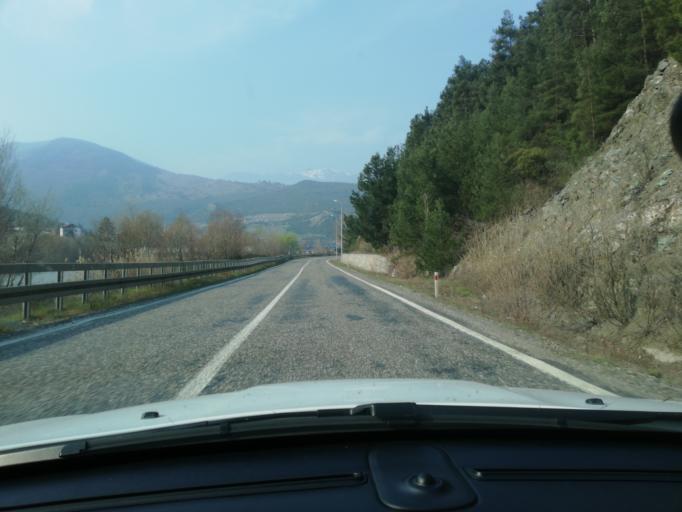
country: TR
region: Karabuk
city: Karabuk
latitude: 41.1574
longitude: 32.5429
